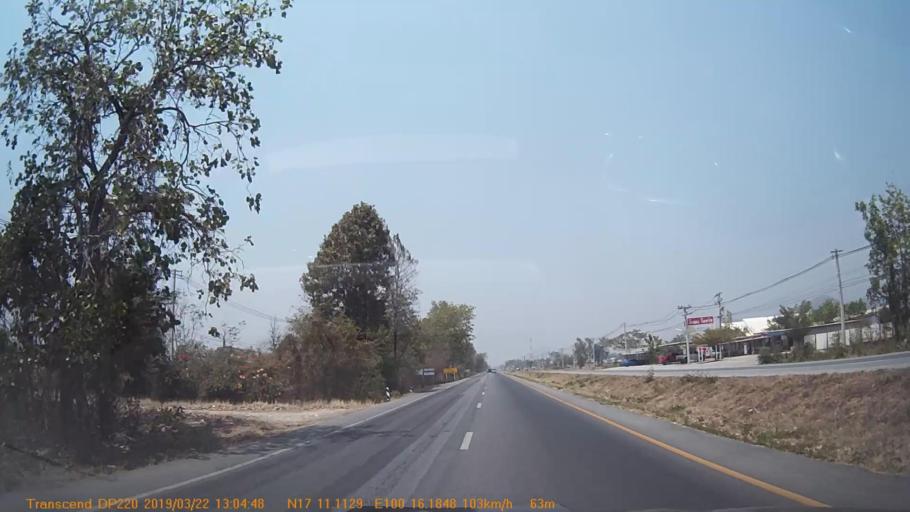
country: TH
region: Phitsanulok
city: Phrom Phiram
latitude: 17.1856
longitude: 100.2696
